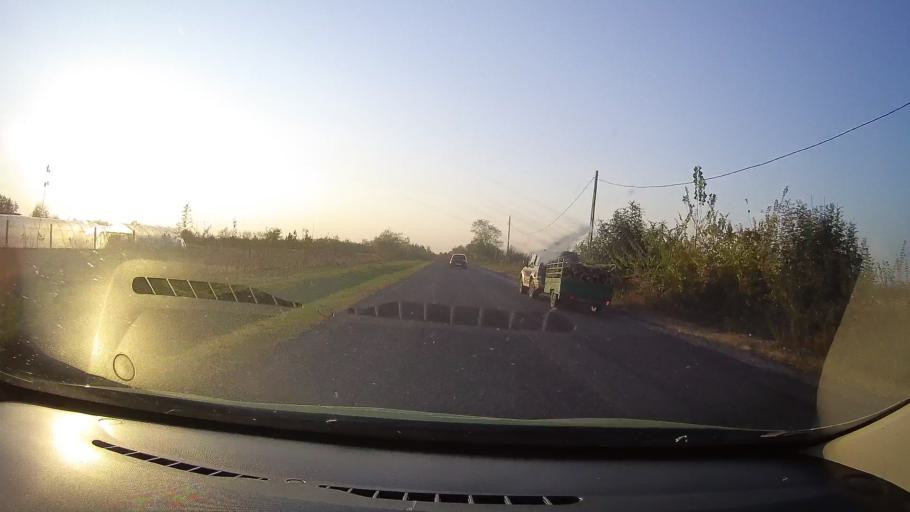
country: RO
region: Arad
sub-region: Comuna Bocsig
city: Bocsig
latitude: 46.4176
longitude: 21.9812
